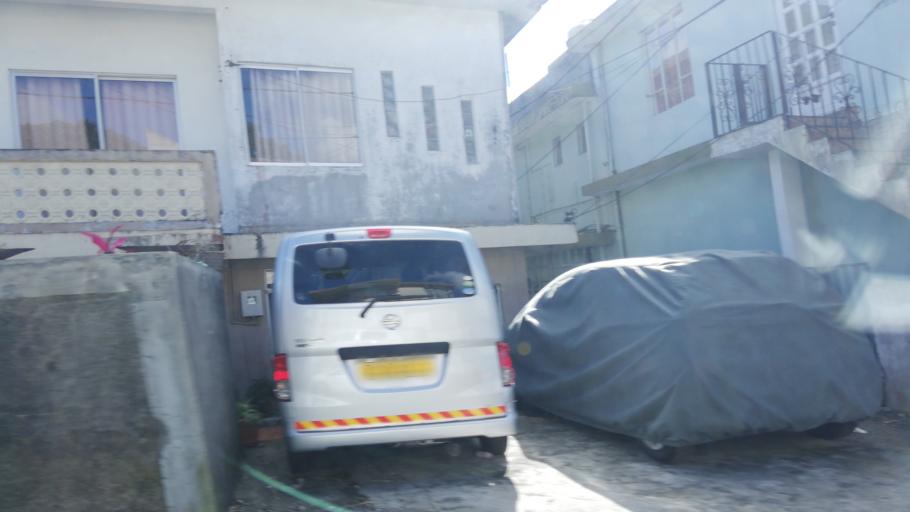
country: MU
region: Moka
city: Quartier Militaire
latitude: -20.2451
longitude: 57.5962
